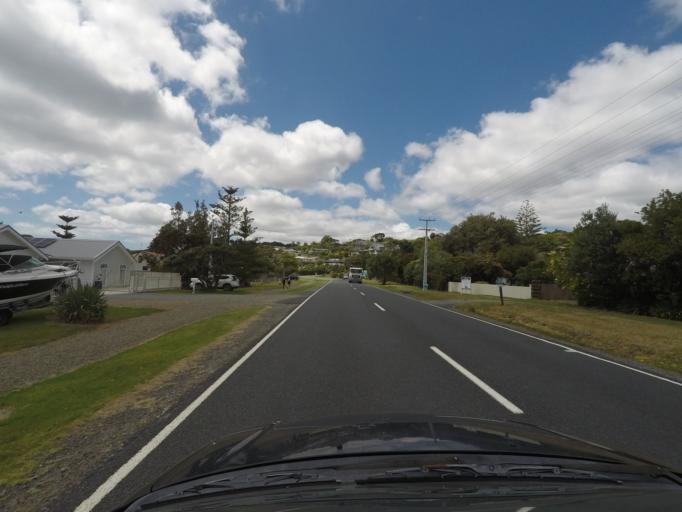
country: NZ
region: Northland
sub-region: Whangarei
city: Ruakaka
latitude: -36.0273
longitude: 174.5024
